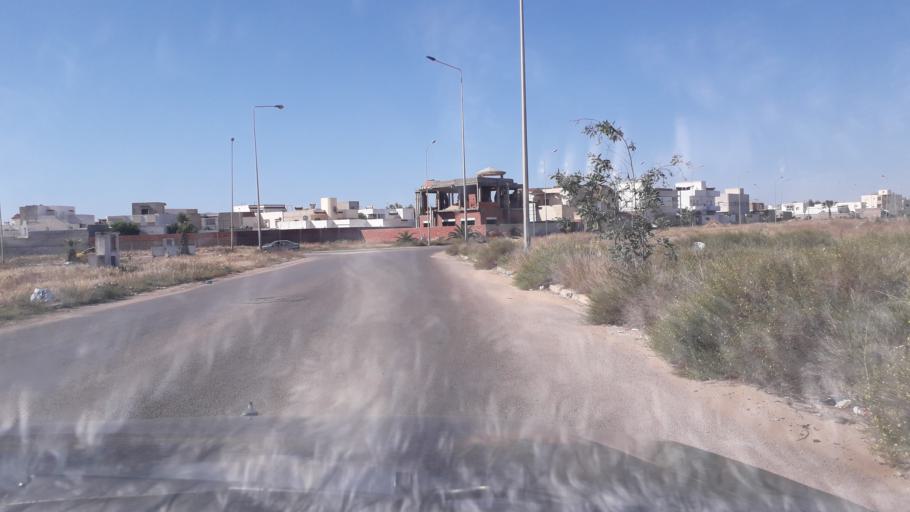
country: TN
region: Safaqis
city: Al Qarmadah
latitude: 34.8288
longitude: 10.7534
